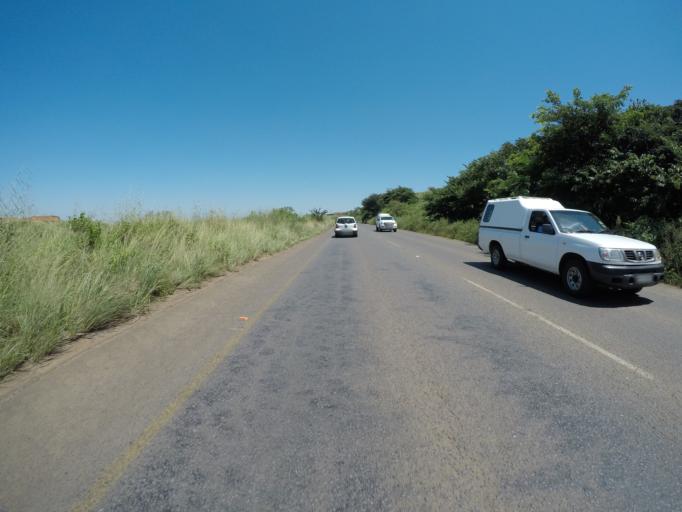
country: ZA
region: KwaZulu-Natal
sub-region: uThungulu District Municipality
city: Empangeni
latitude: -28.7526
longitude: 31.8766
